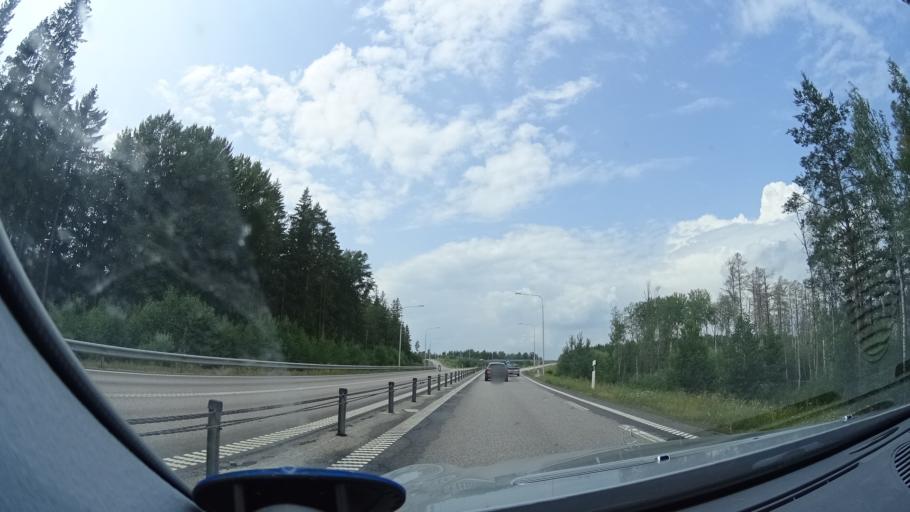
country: SE
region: Kalmar
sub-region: Nybro Kommun
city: Nybro
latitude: 56.7267
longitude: 15.8928
